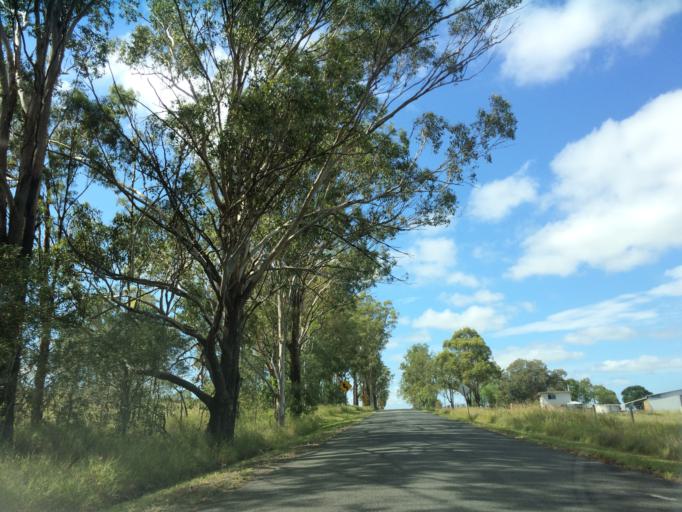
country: AU
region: Queensland
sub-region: Logan
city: Cedar Vale
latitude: -27.8845
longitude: 152.9722
